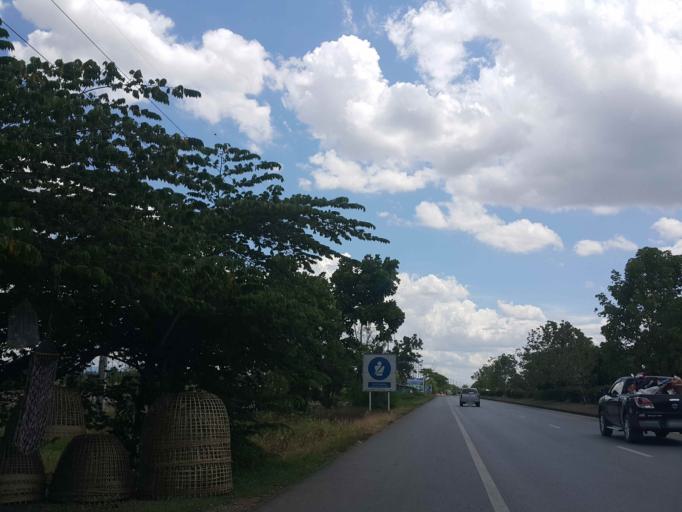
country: TH
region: Phrae
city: Nong Muang Khai
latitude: 18.2560
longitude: 100.2316
